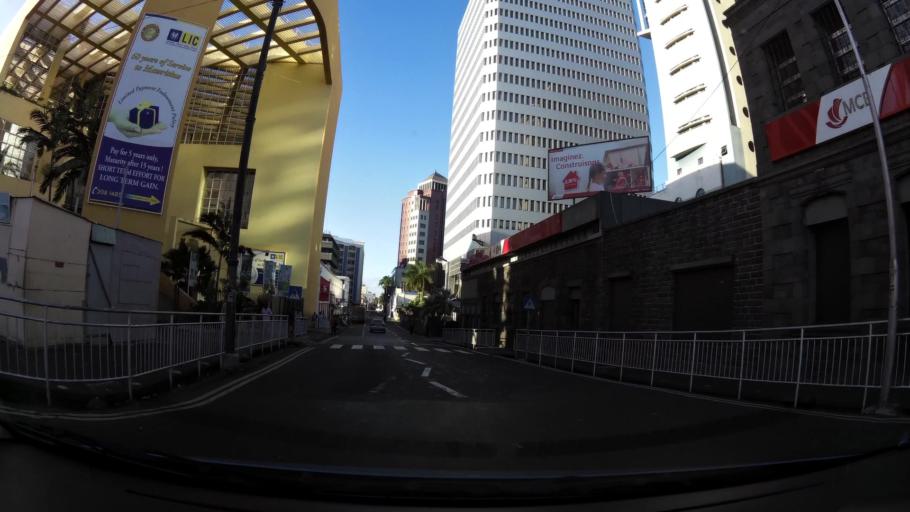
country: MU
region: Port Louis
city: Port Louis
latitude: -20.1633
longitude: 57.4998
